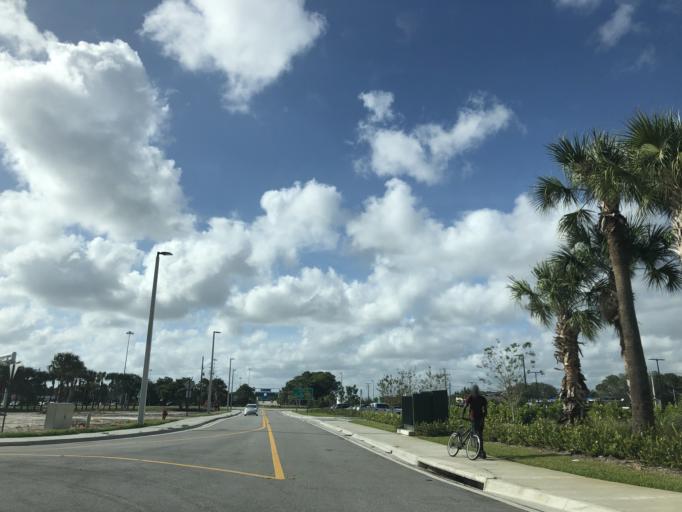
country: US
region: Florida
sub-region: Palm Beach County
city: West Palm Beach
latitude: 26.6894
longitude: -80.0773
